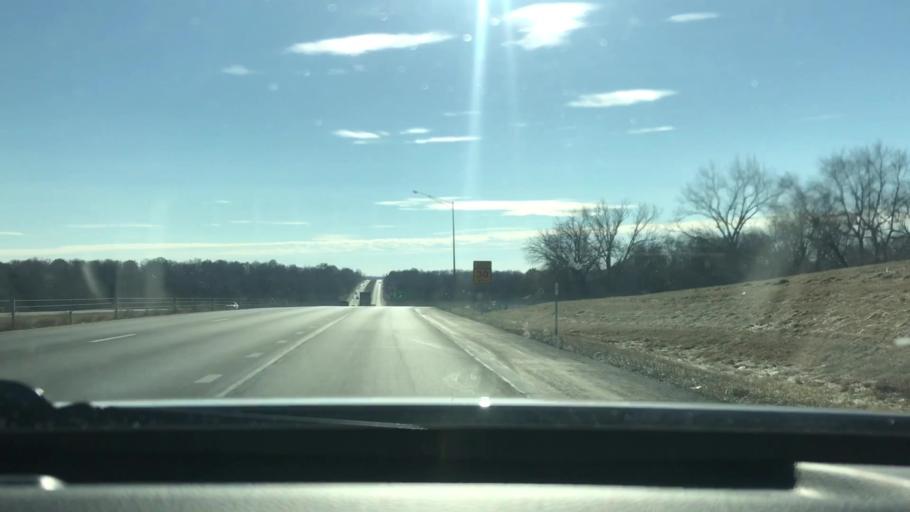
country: US
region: Missouri
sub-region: Clay County
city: Gladstone
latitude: 39.2210
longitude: -94.5895
